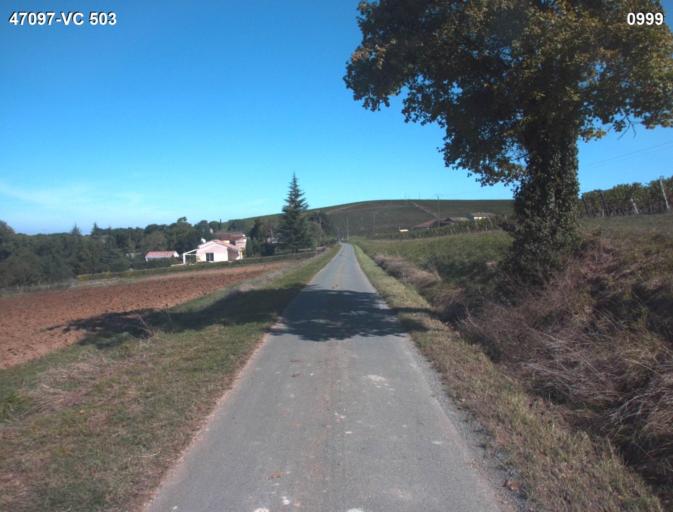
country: FR
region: Aquitaine
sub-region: Departement du Lot-et-Garonne
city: Vianne
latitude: 44.2007
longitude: 0.3707
